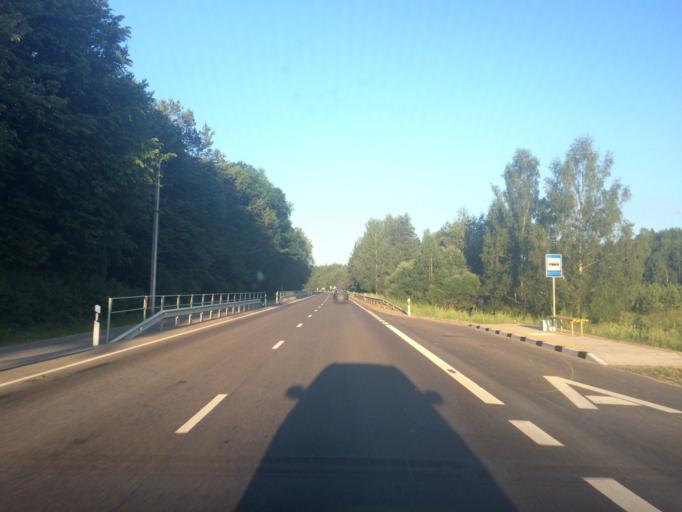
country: LT
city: Zarasai
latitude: 55.6950
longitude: 26.1479
